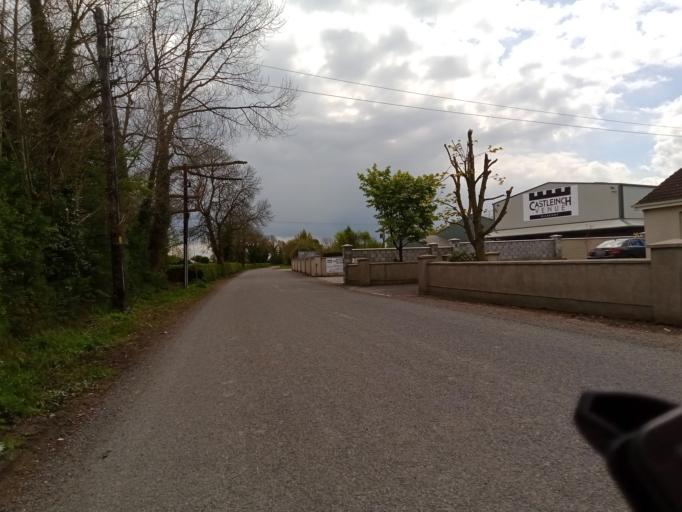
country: IE
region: Leinster
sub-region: Kilkenny
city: Kilkenny
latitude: 52.6159
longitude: -7.2944
